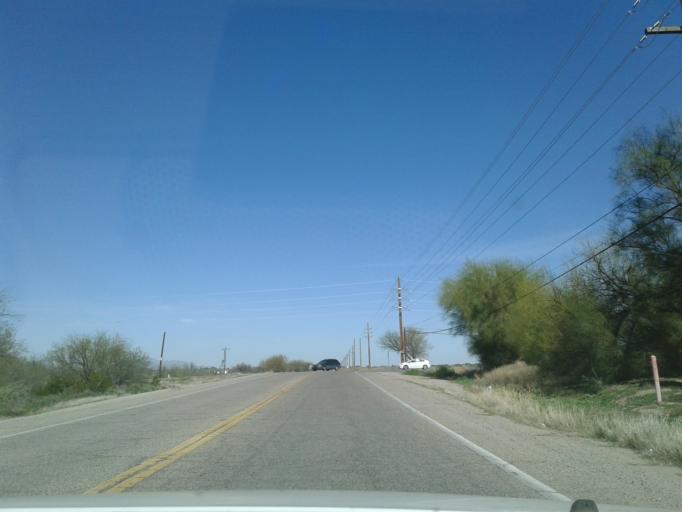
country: US
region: Arizona
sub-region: Pima County
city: Avra Valley
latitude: 32.4502
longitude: -111.3043
